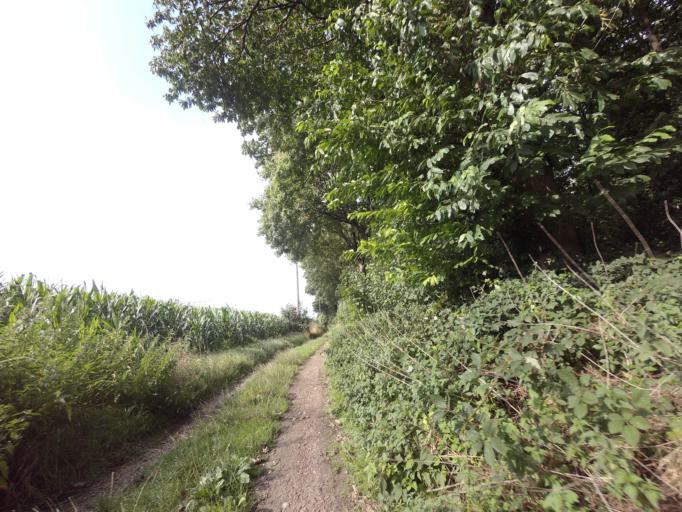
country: BE
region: Flanders
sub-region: Provincie Vlaams-Brabant
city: Grimbergen
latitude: 50.9313
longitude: 4.3993
